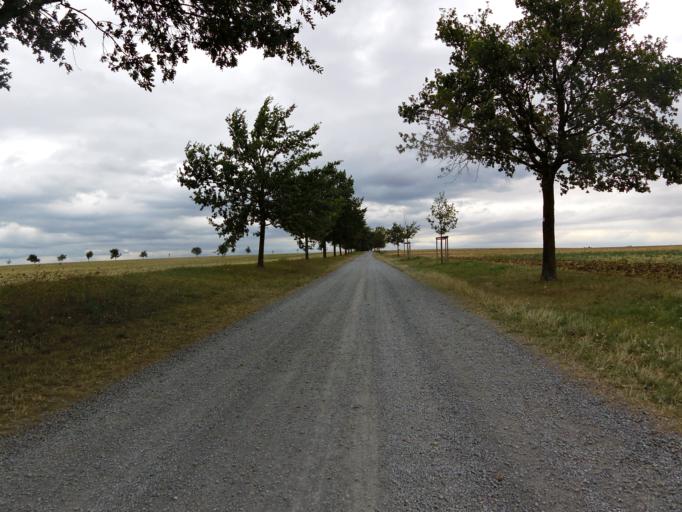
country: DE
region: Bavaria
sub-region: Regierungsbezirk Unterfranken
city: Wuerzburg
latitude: 49.8191
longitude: 9.9399
